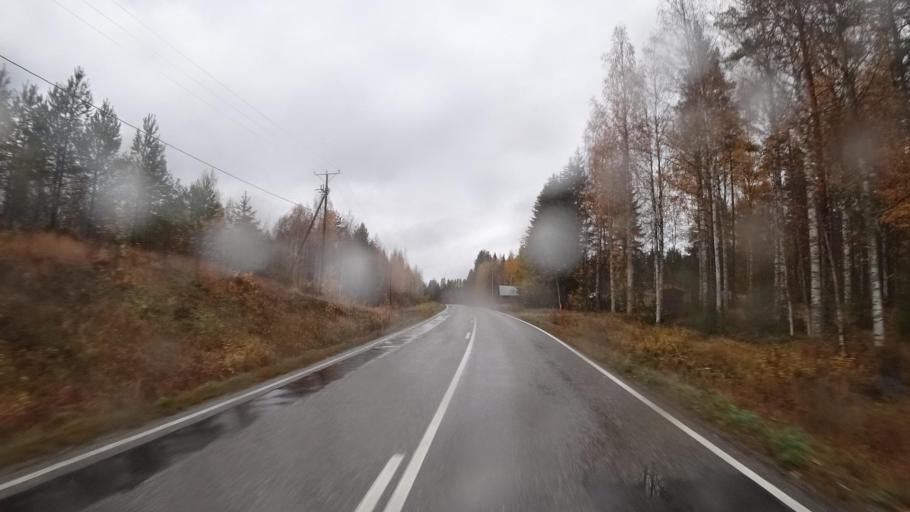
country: FI
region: North Karelia
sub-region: Joensuu
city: Outokumpu
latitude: 62.6271
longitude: 28.9158
